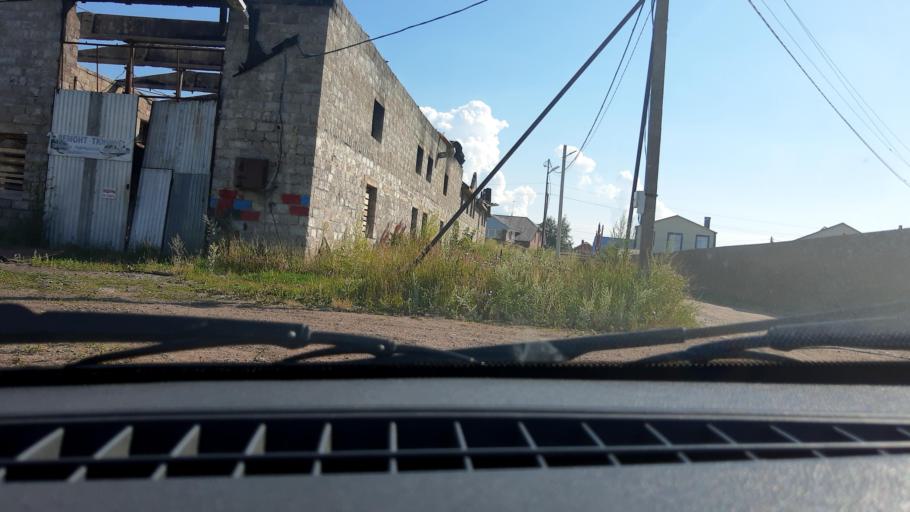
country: RU
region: Bashkortostan
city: Mikhaylovka
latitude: 54.8036
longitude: 55.8777
